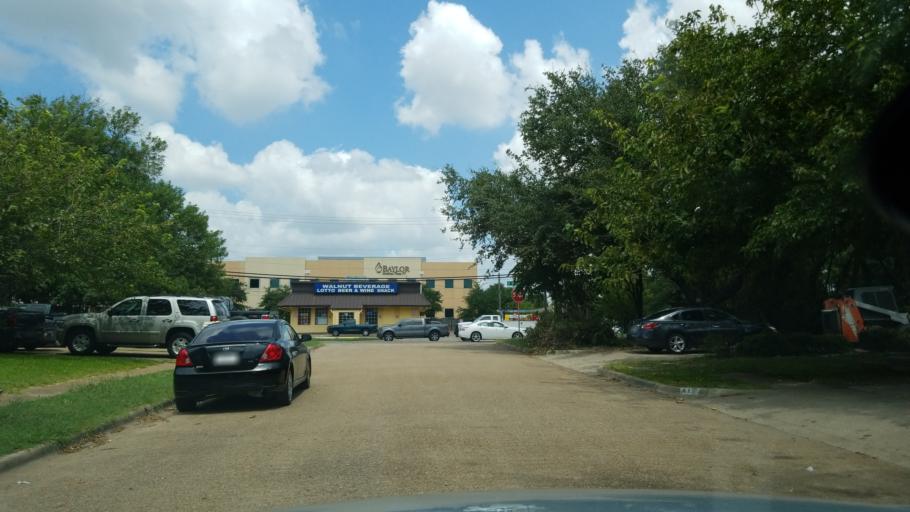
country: US
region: Texas
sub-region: Dallas County
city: Garland
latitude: 32.9159
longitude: -96.6610
